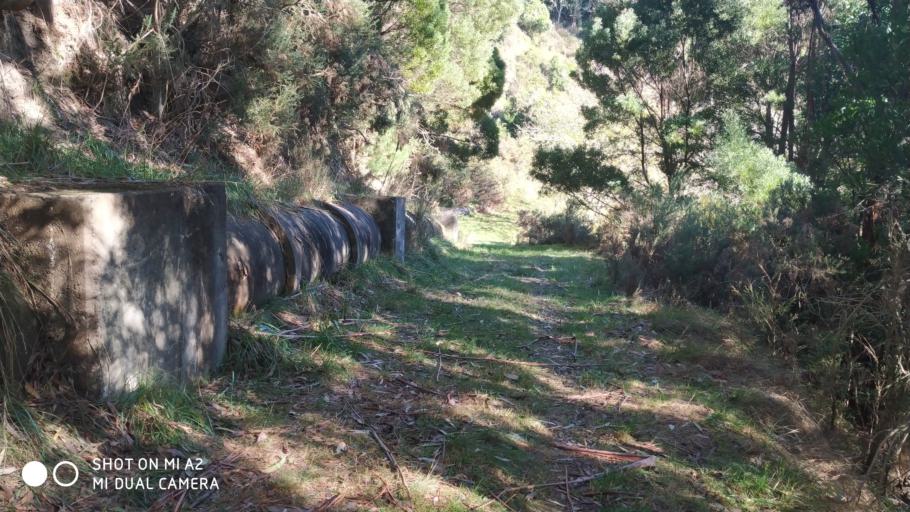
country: NZ
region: Nelson
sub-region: Nelson City
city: Nelson
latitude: -41.2935
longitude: 173.3197
